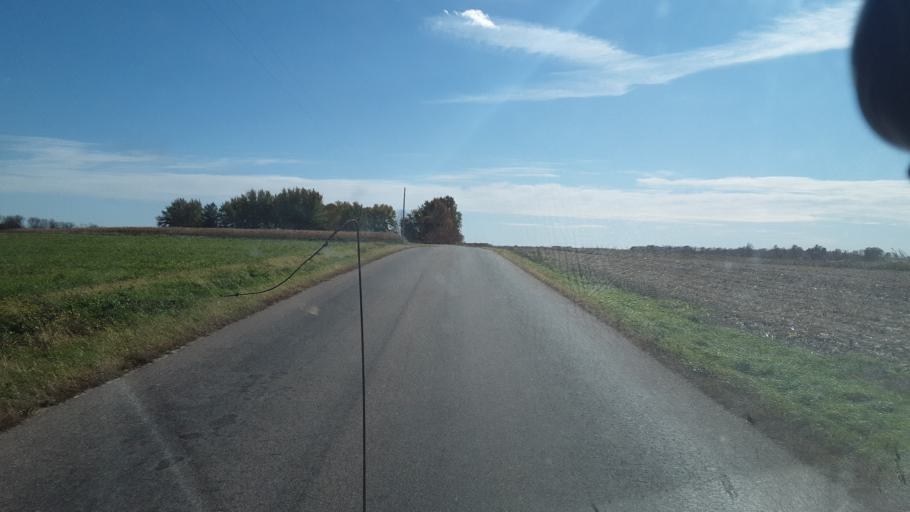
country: US
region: Wisconsin
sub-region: Vernon County
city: Hillsboro
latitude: 43.6959
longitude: -90.4427
